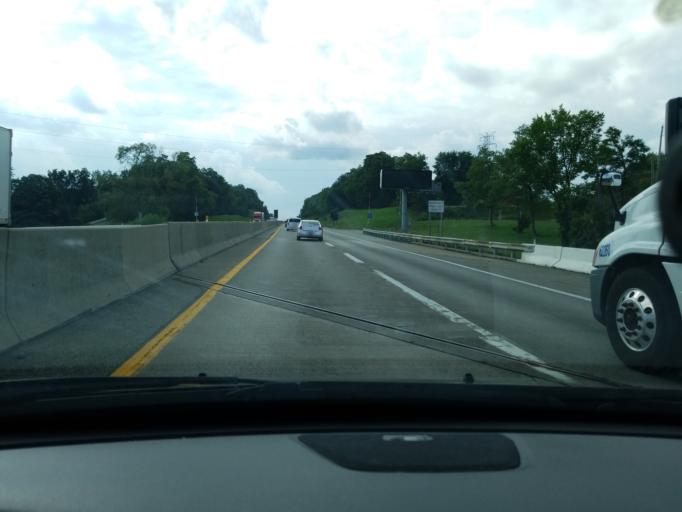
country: US
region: Pennsylvania
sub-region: Beaver County
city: Beaver Falls
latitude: 40.7929
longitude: -80.2743
